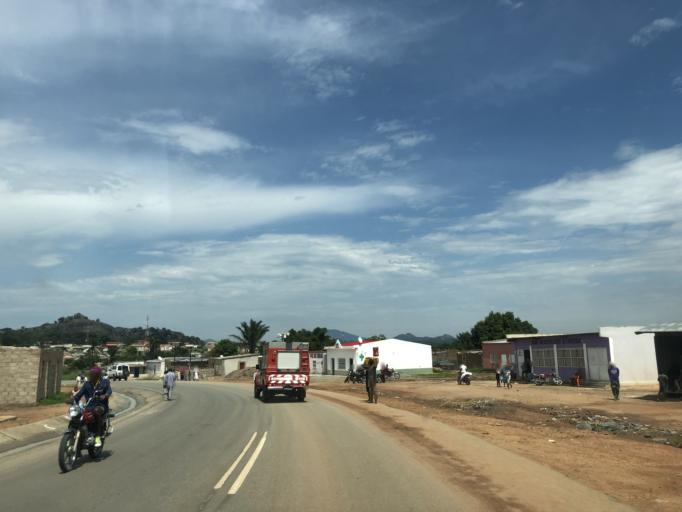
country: AO
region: Cuanza Sul
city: Quibala
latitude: -10.7356
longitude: 14.9873
